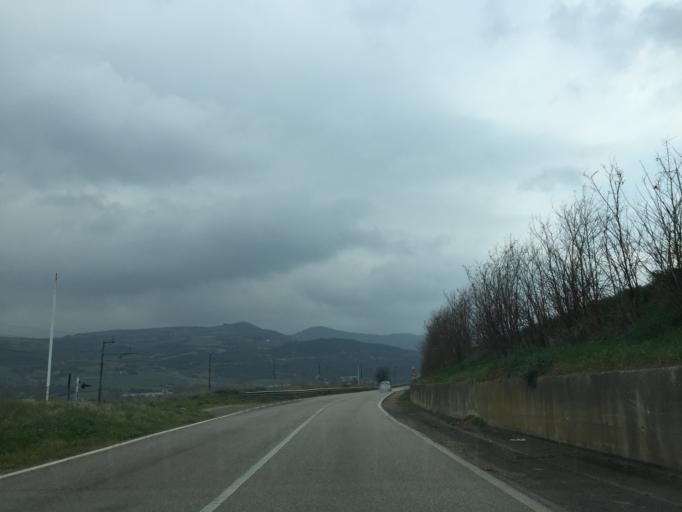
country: IT
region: Apulia
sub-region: Provincia di Foggia
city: Bovino
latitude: 41.2827
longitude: 15.3785
